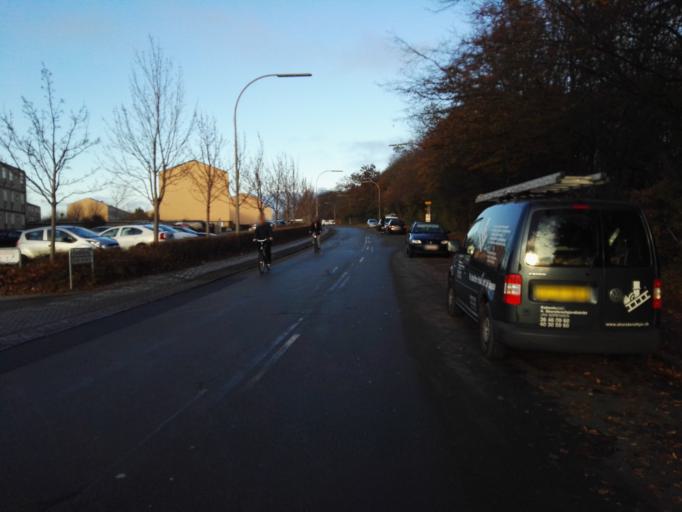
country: DK
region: Capital Region
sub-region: Herlev Kommune
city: Herlev
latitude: 55.7174
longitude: 12.4133
